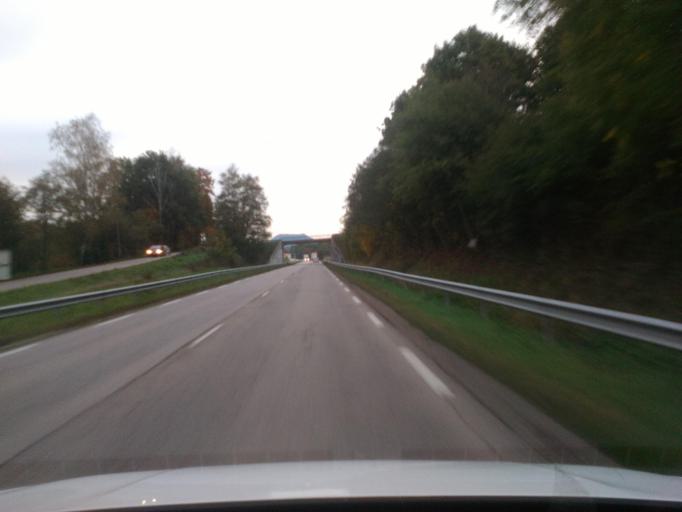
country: FR
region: Lorraine
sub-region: Departement des Vosges
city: Ban-de-Laveline
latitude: 48.2721
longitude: 7.0505
